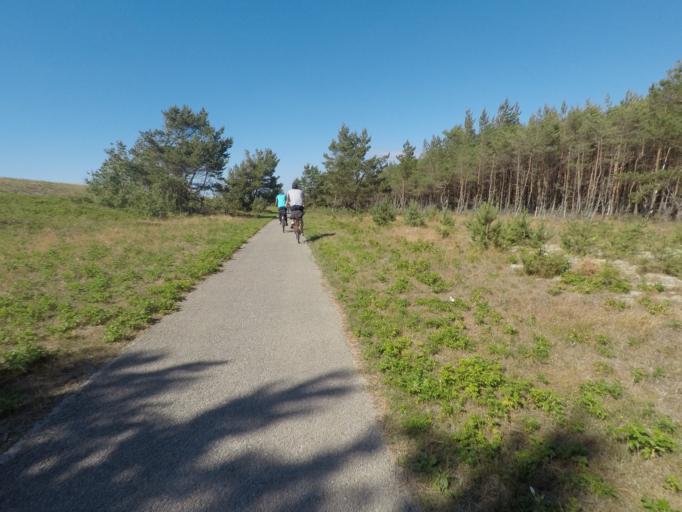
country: LT
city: Neringa
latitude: 55.5129
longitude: 21.0930
